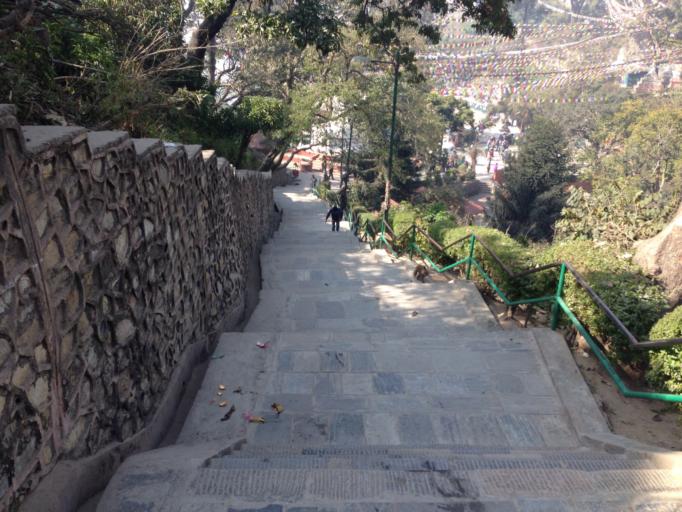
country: NP
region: Central Region
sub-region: Bagmati Zone
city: Kathmandu
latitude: 27.7157
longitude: 85.2903
